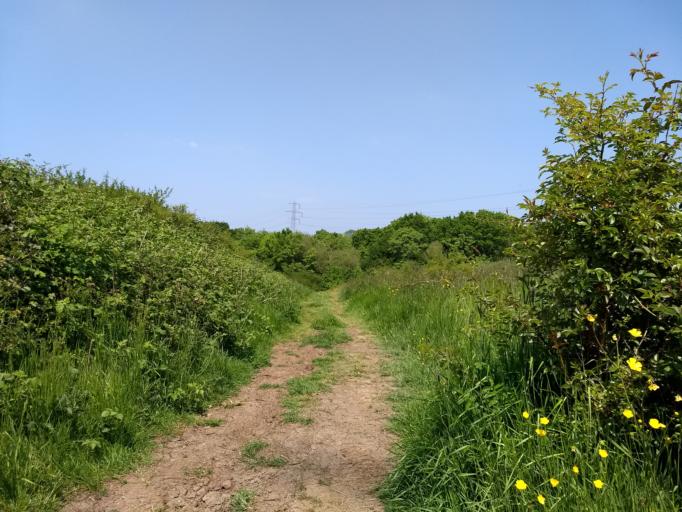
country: GB
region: England
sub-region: Isle of Wight
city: East Cowes
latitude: 50.7359
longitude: -1.2778
